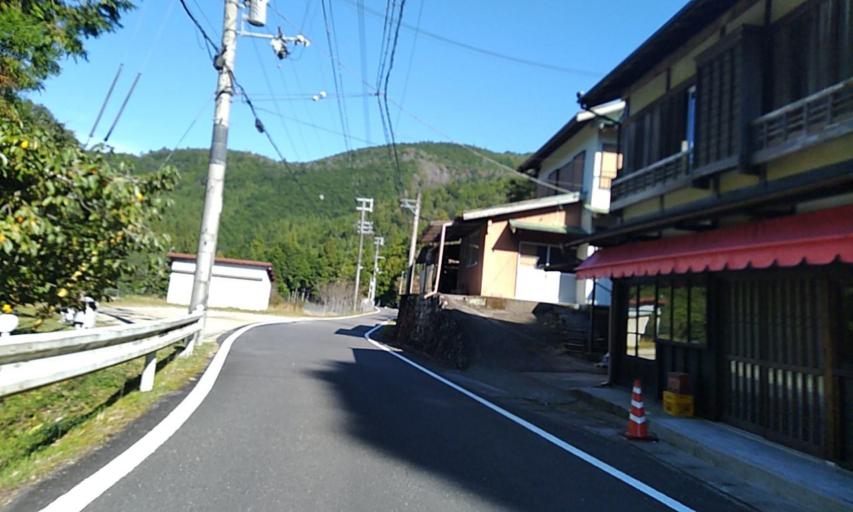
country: JP
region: Wakayama
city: Shingu
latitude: 33.9294
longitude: 135.9795
